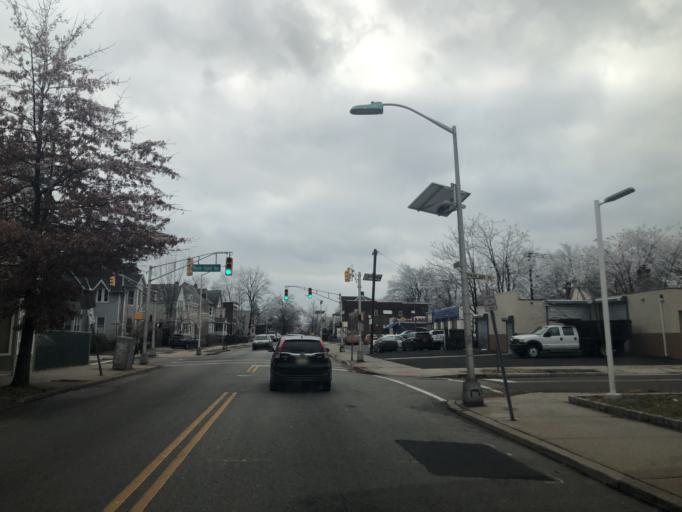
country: US
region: New Jersey
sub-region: Essex County
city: Orange
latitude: 40.7550
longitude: -74.2283
